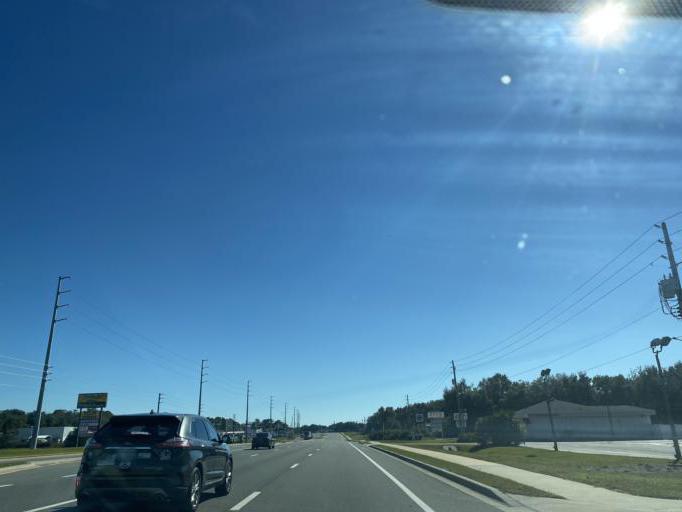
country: US
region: Florida
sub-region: Lake County
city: Fruitland Park
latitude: 28.8493
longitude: -81.9004
